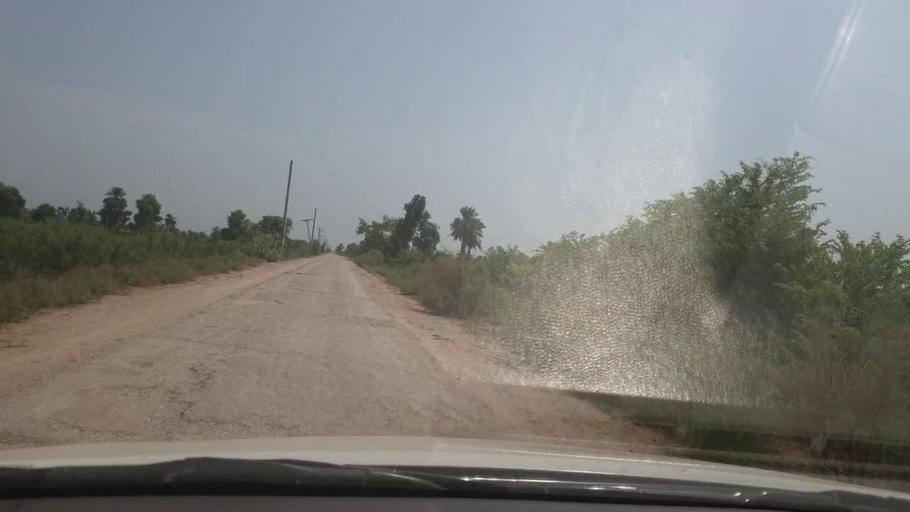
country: PK
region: Sindh
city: Garhi Yasin
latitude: 27.9754
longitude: 68.5032
